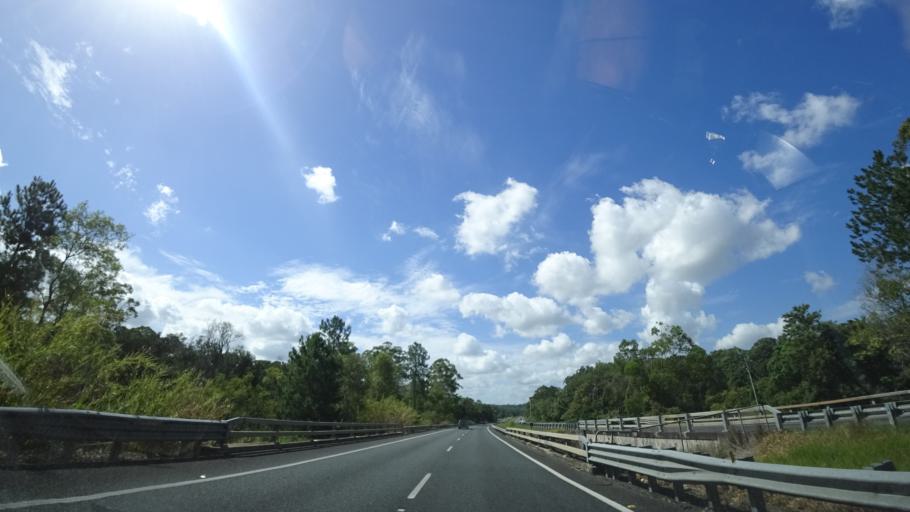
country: AU
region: Queensland
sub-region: Sunshine Coast
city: Woombye
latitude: -26.6513
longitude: 152.9901
